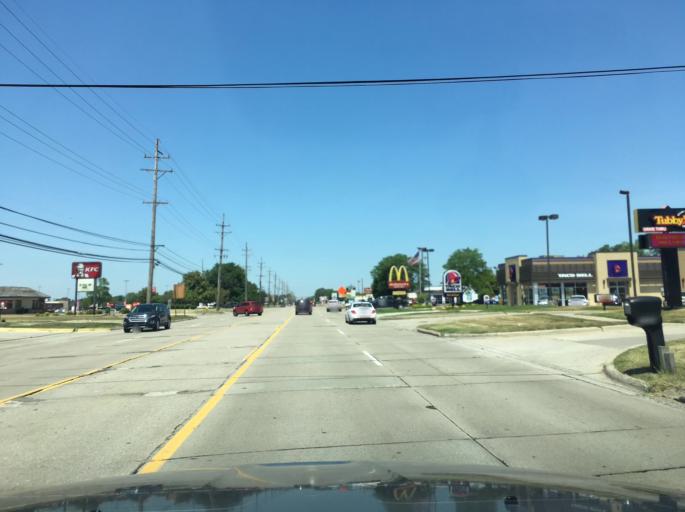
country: US
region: Michigan
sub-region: Macomb County
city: Clinton
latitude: 42.6008
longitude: -82.9525
